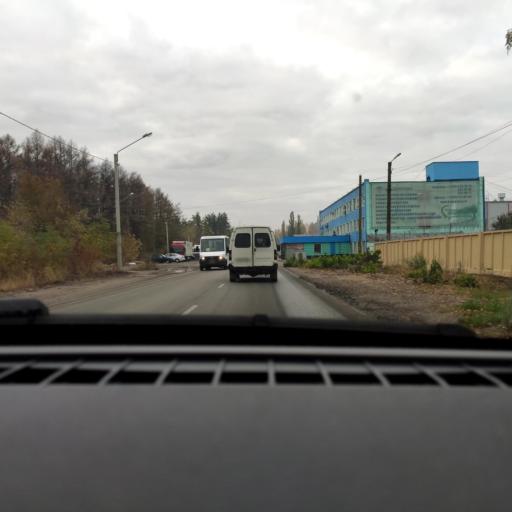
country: RU
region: Voronezj
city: Somovo
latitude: 51.7212
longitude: 39.2951
